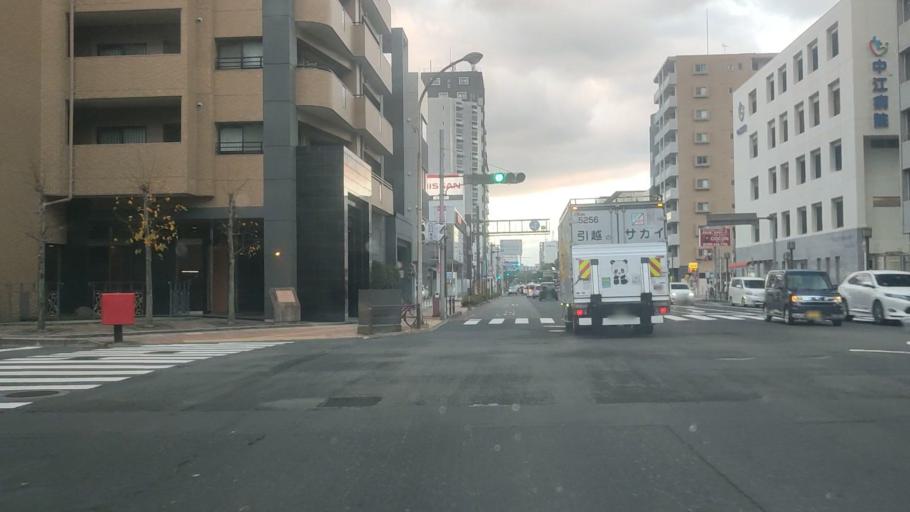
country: JP
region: Kagoshima
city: Kagoshima-shi
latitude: 31.5894
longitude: 130.5467
